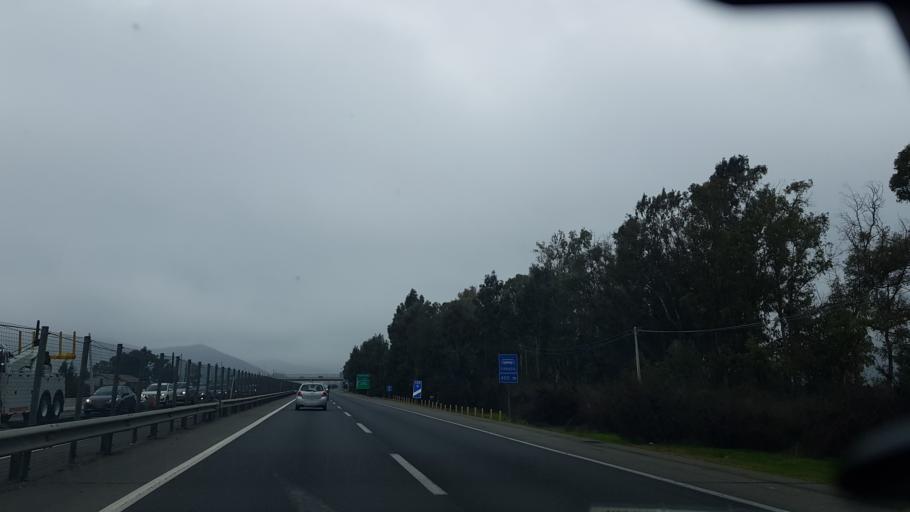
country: CL
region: Santiago Metropolitan
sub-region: Provincia de Santiago
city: Lo Prado
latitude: -33.4484
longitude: -70.8684
